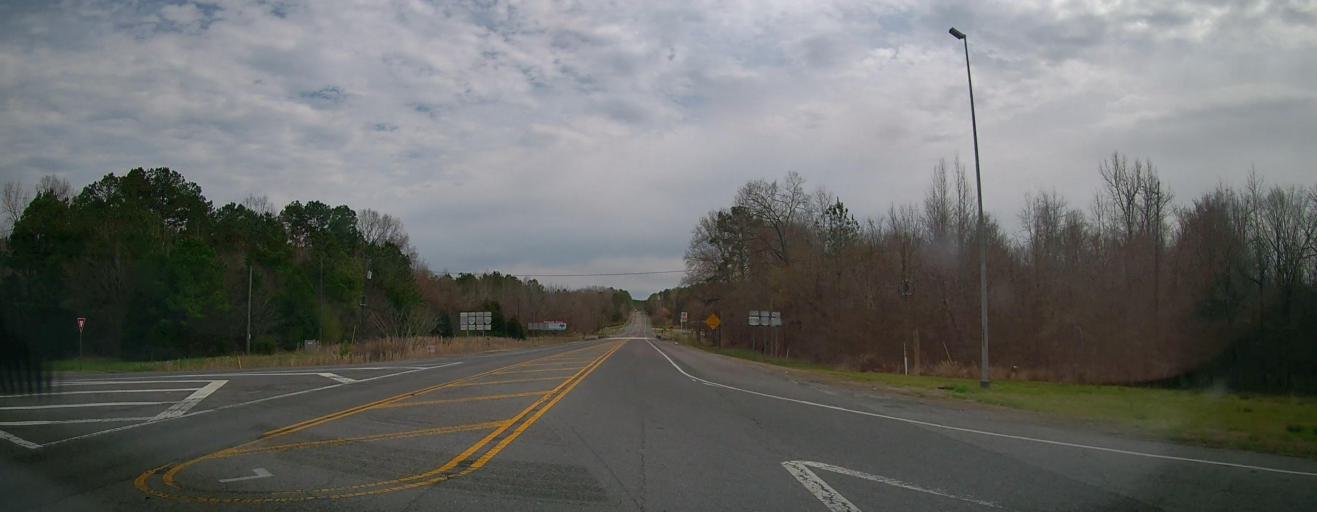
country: US
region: Alabama
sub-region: Marion County
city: Hamilton
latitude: 34.0710
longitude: -87.9750
